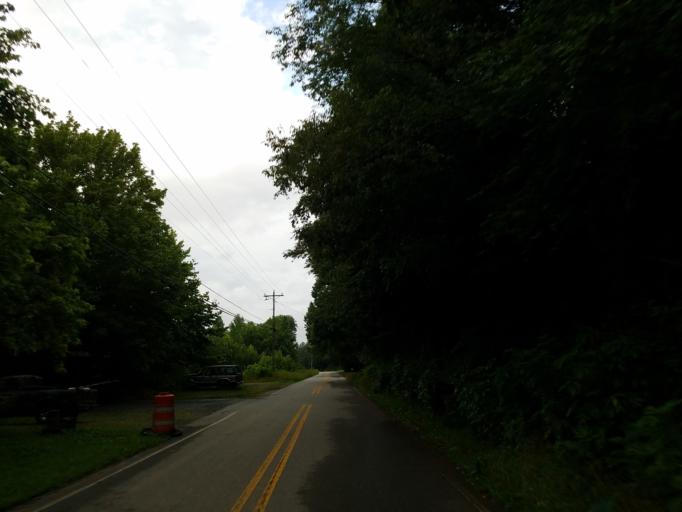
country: US
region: Georgia
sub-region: Fannin County
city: Blue Ridge
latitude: 34.8370
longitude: -84.3465
